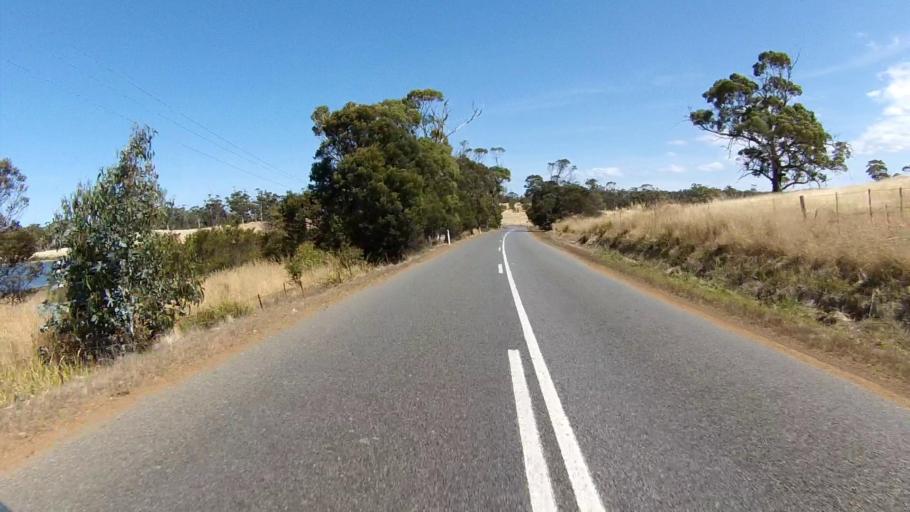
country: AU
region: Tasmania
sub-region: Sorell
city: Sorell
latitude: -42.2793
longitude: 148.0018
